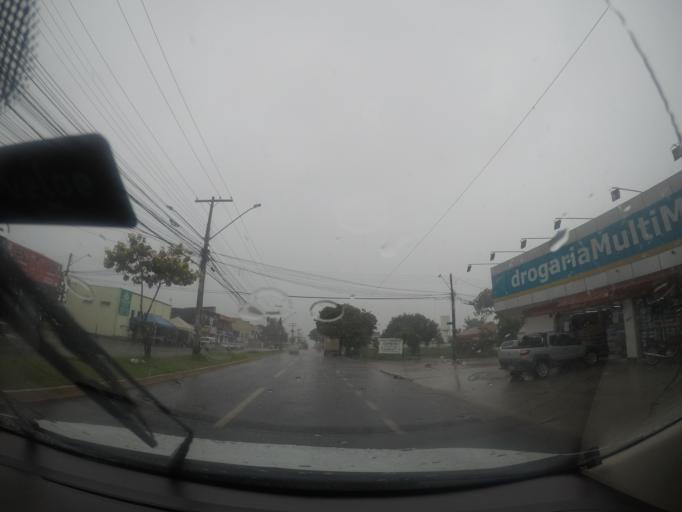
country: BR
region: Goias
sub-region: Goiania
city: Goiania
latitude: -16.6167
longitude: -49.3507
